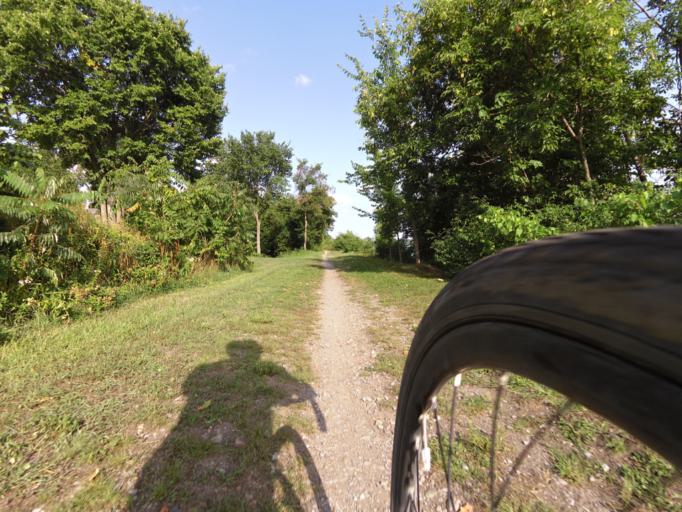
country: CA
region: Ontario
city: Kingston
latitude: 44.4234
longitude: -76.5703
